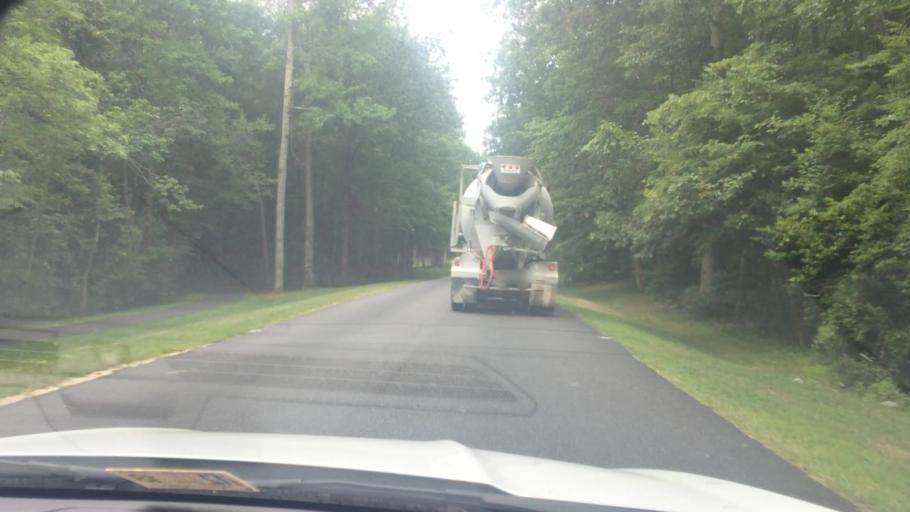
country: US
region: Virginia
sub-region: James City County
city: Williamsburg
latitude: 37.2937
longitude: -76.7902
